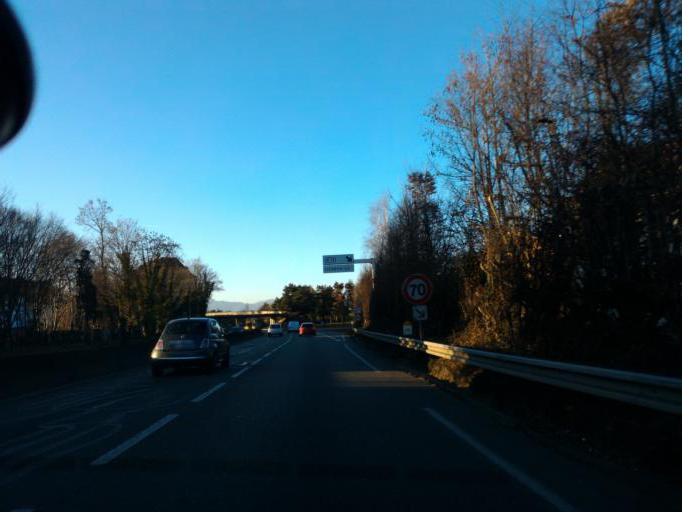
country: FR
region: Alsace
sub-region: Departement du Haut-Rhin
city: Illzach
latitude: 47.7638
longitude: 7.3499
